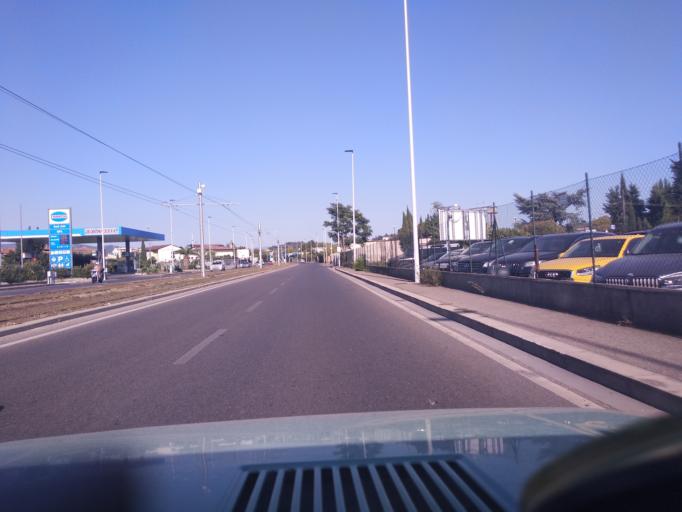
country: IT
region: Tuscany
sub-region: Province of Florence
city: Scandicci
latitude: 43.7646
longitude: 11.2016
